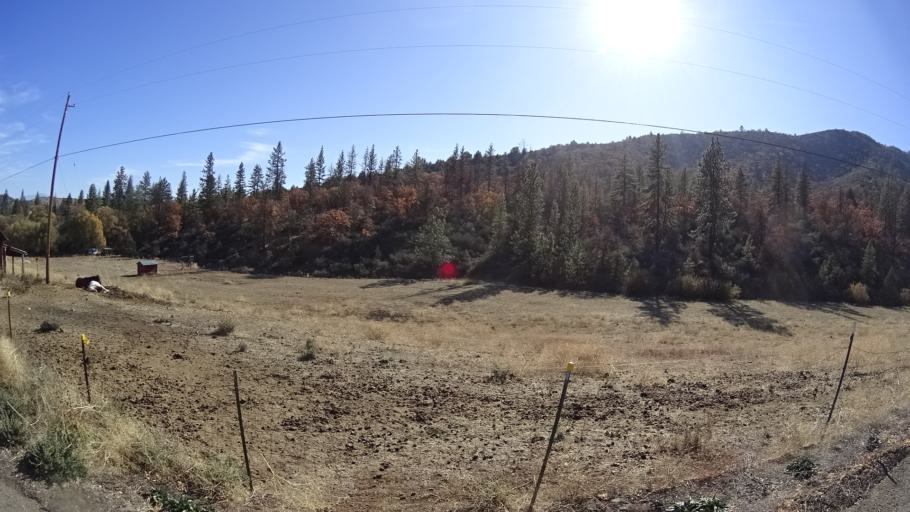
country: US
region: California
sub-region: Siskiyou County
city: Yreka
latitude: 41.7616
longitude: -122.6385
